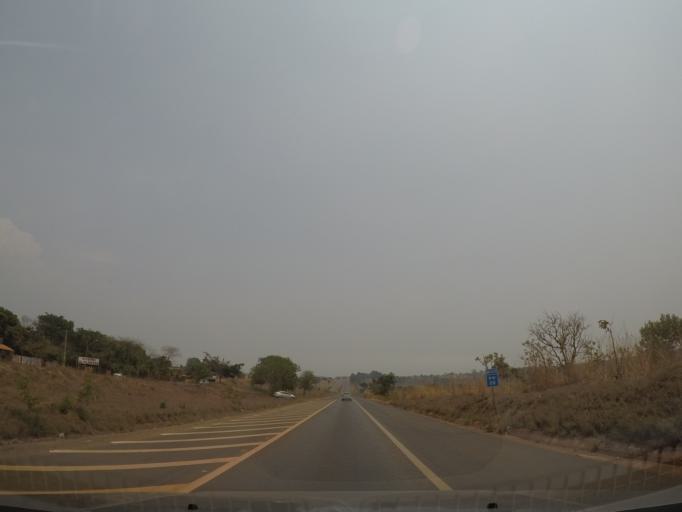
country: BR
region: Federal District
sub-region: Brasilia
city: Brasilia
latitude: -15.7386
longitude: -48.3908
